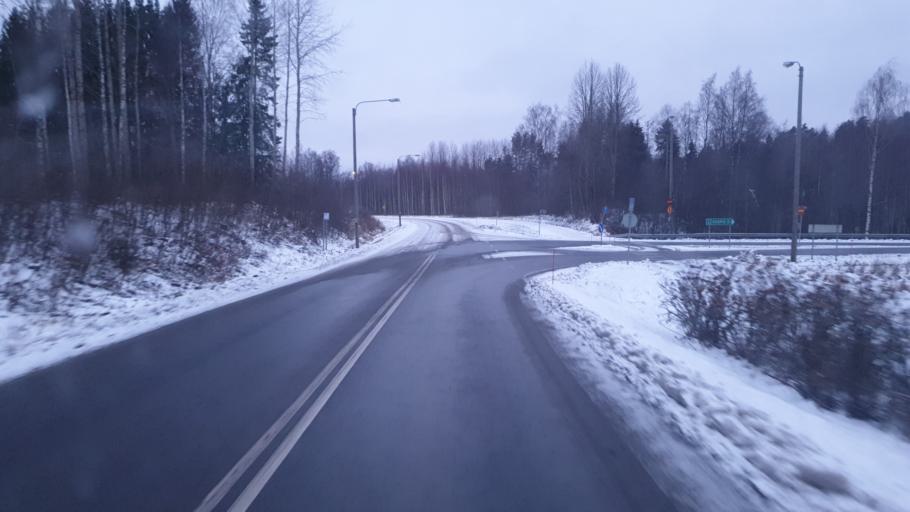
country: FI
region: Northern Savo
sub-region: Kuopio
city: Siilinjaervi
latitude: 63.0593
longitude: 27.6690
